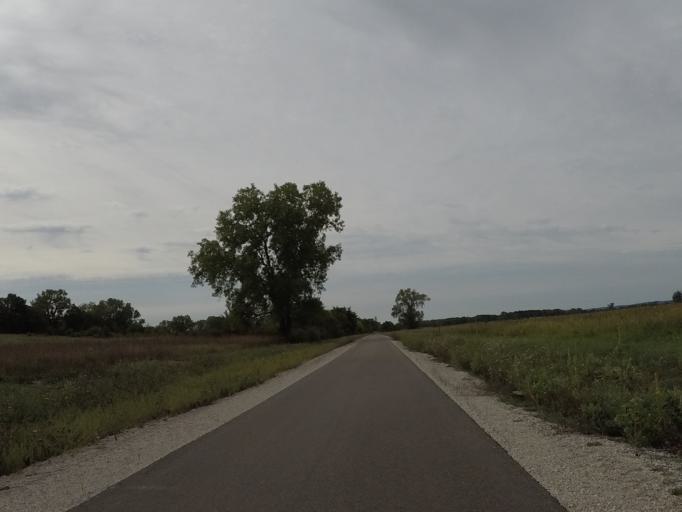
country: US
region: Wisconsin
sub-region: Sauk County
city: Prairie du Sac
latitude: 43.3768
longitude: -89.7353
